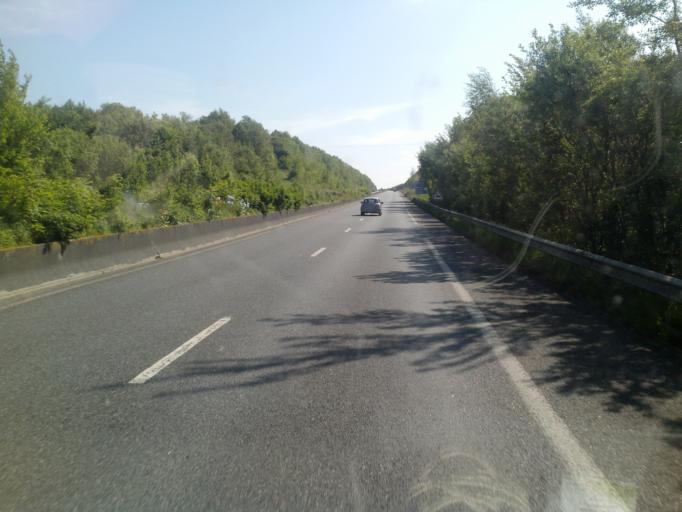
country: FR
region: Picardie
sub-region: Departement de la Somme
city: Abbeville
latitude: 50.1043
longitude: 1.7849
